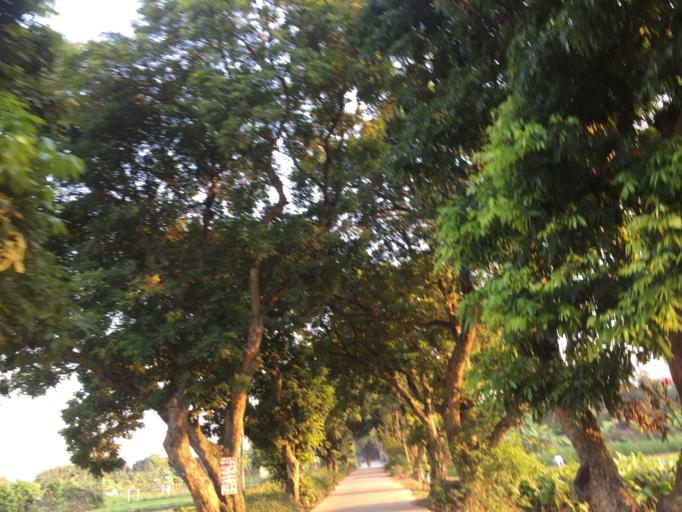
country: VN
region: Ha Noi
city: Chuc Son
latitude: 20.9076
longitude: 105.7234
